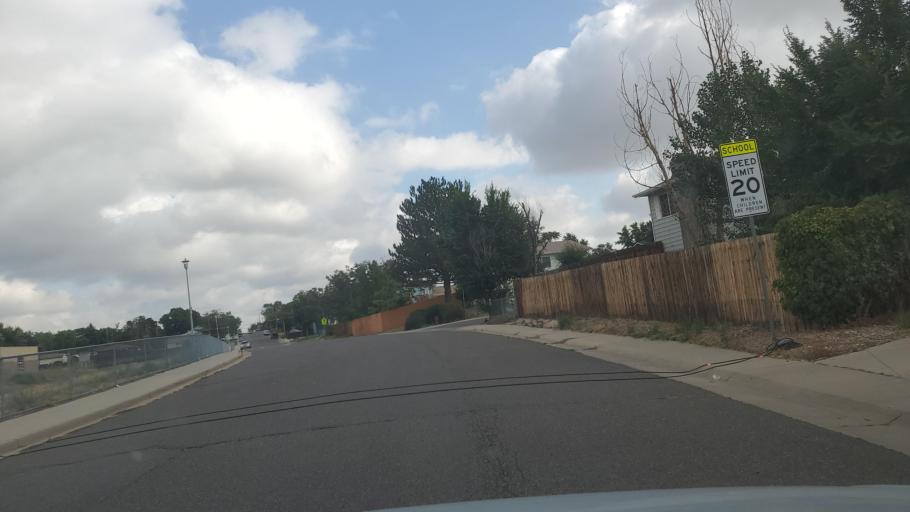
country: US
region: Colorado
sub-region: Adams County
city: Welby
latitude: 39.8468
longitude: -104.9684
